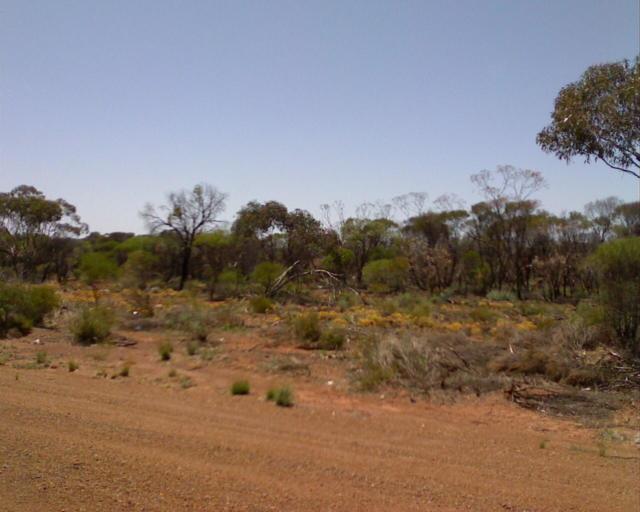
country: AU
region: Western Australia
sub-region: Kalgoorlie/Boulder
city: Kalgoorlie
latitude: -31.1066
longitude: 120.7382
